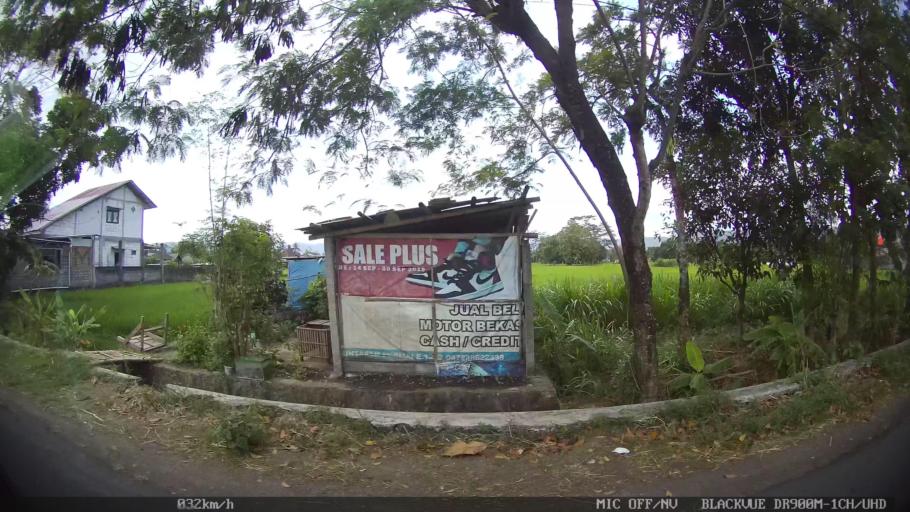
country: ID
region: Daerah Istimewa Yogyakarta
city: Depok
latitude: -7.8189
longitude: 110.4646
